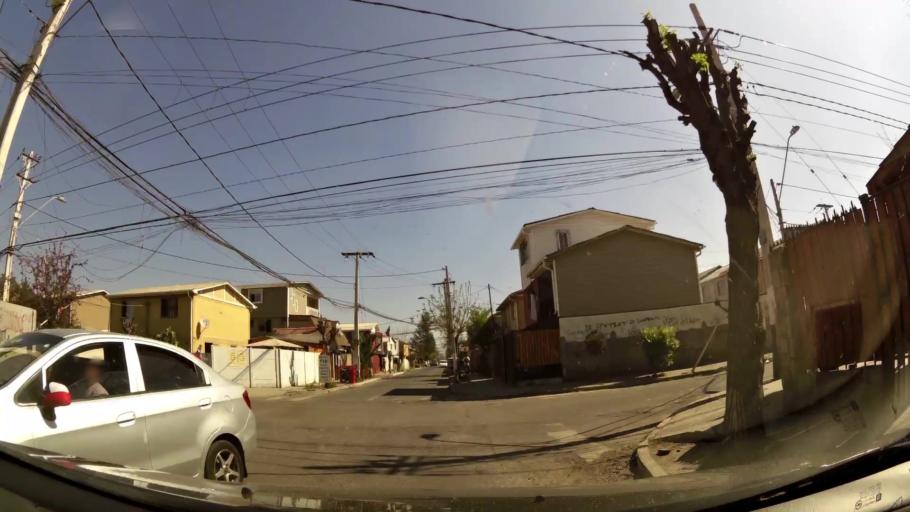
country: CL
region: Santiago Metropolitan
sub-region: Provincia de Santiago
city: Lo Prado
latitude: -33.3502
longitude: -70.7455
